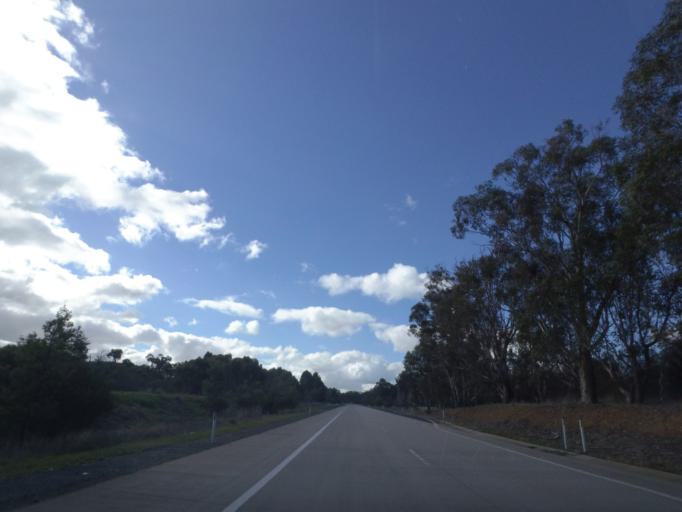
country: AU
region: New South Wales
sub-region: Greater Hume Shire
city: Holbrook
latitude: -35.8833
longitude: 147.1761
